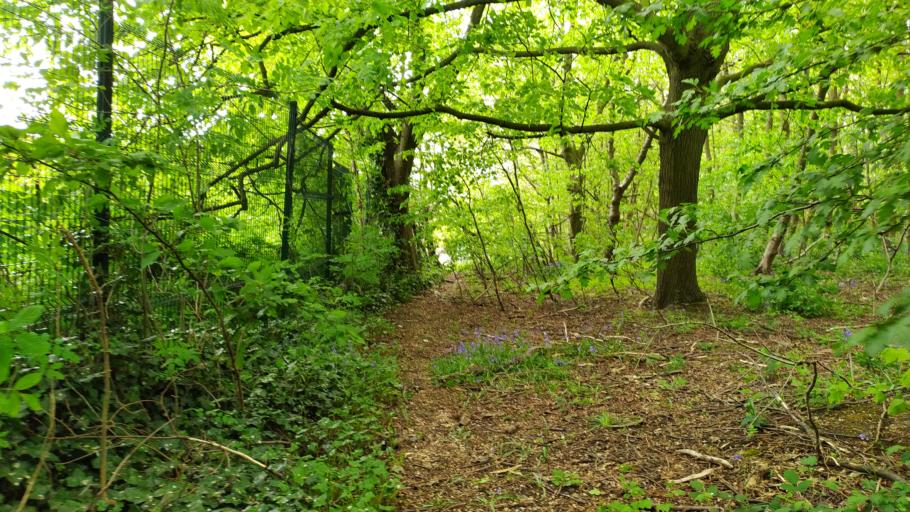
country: GB
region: England
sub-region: City and Borough of Leeds
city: Shadwell
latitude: 53.8062
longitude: -1.4805
